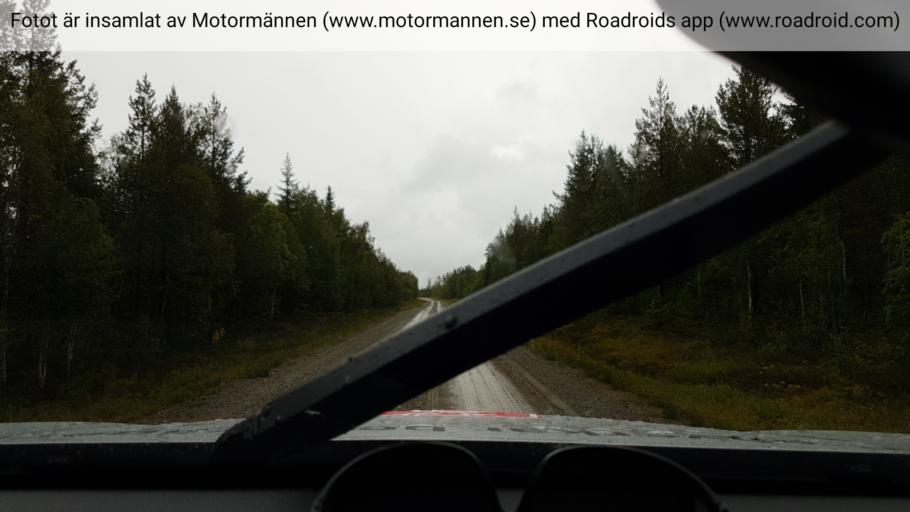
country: SE
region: Vaesterbotten
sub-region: Asele Kommun
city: Insjon
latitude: 64.7847
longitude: 17.5803
